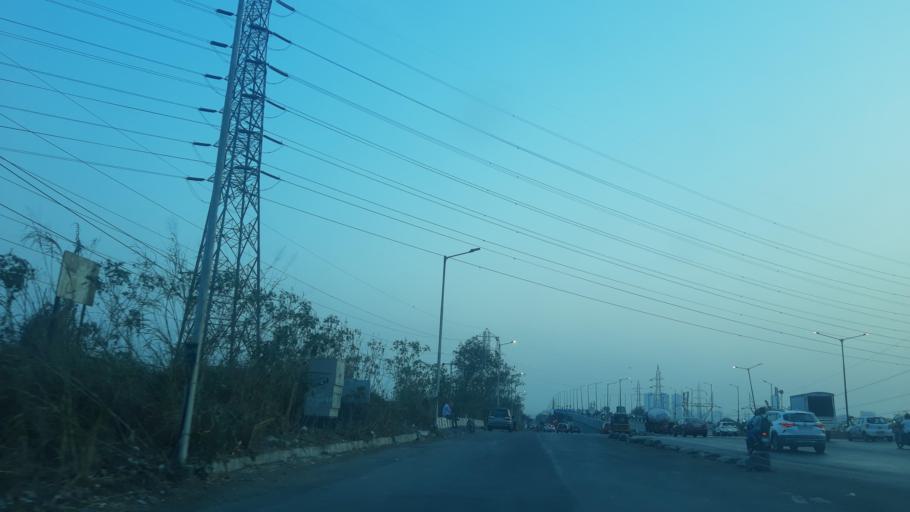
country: IN
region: Maharashtra
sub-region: Thane
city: Airoli
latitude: 19.1578
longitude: 72.9594
